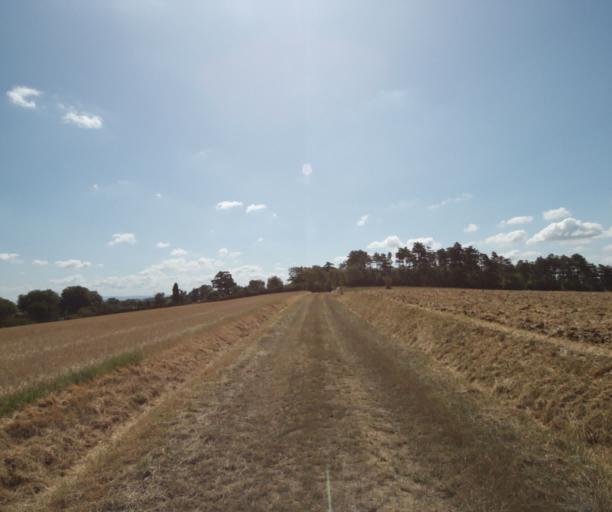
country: FR
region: Midi-Pyrenees
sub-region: Departement de la Haute-Garonne
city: Auriac-sur-Vendinelle
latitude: 43.4669
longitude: 1.7918
